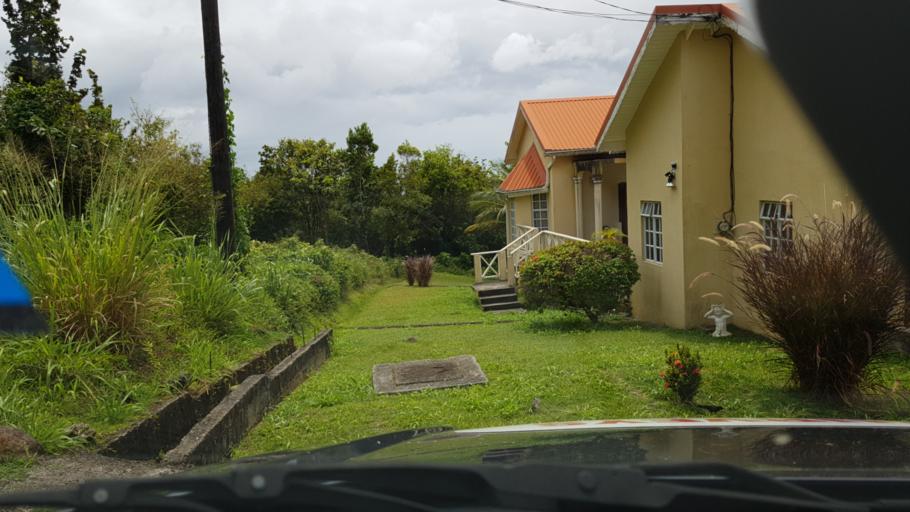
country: LC
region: Anse-la-Raye
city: Anse La Raye
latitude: 13.9481
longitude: -61.0354
